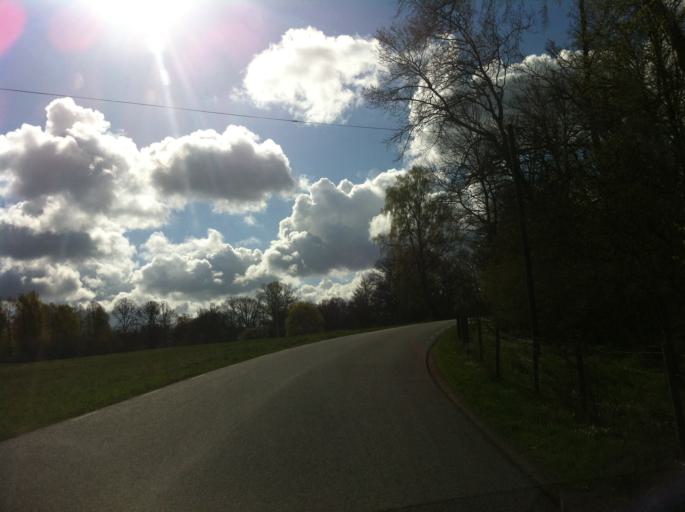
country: SE
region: Skane
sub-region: Hoors Kommun
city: Satofta
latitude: 55.9081
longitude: 13.5771
